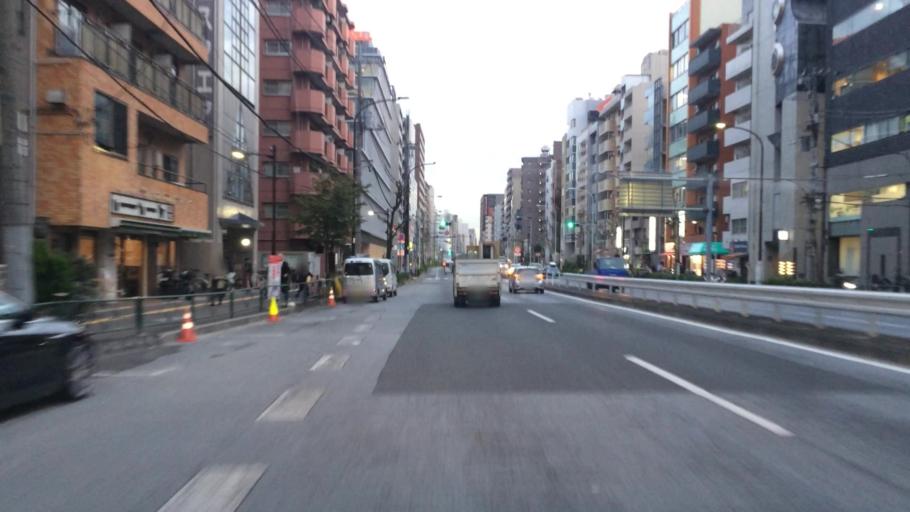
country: JP
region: Tokyo
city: Tokyo
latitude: 35.6406
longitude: 139.7025
